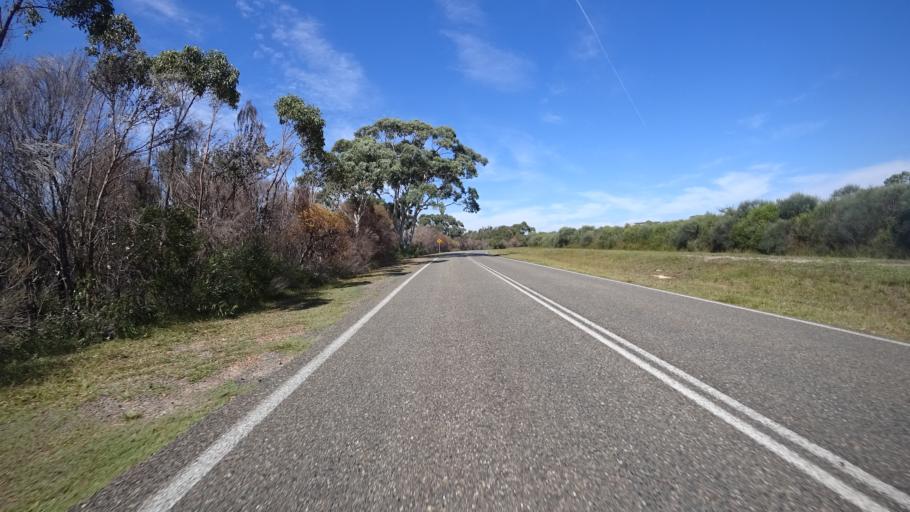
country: AU
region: New South Wales
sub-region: Shoalhaven Shire
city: Falls Creek
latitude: -35.1397
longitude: 150.7050
